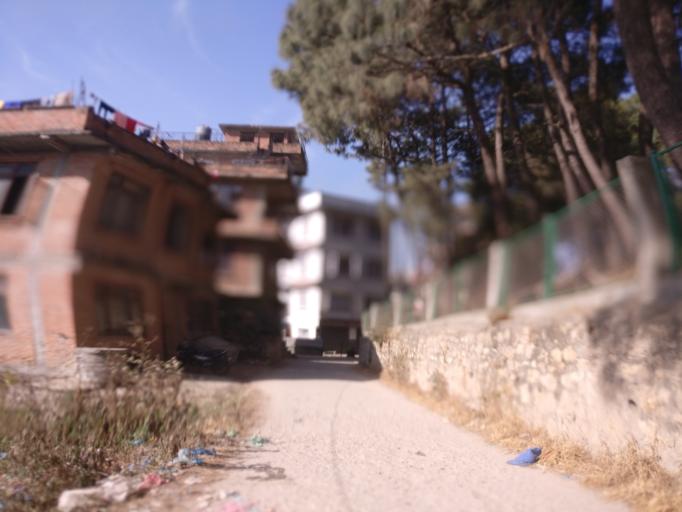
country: NP
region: Central Region
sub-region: Bagmati Zone
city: Patan
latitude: 27.6714
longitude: 85.3333
